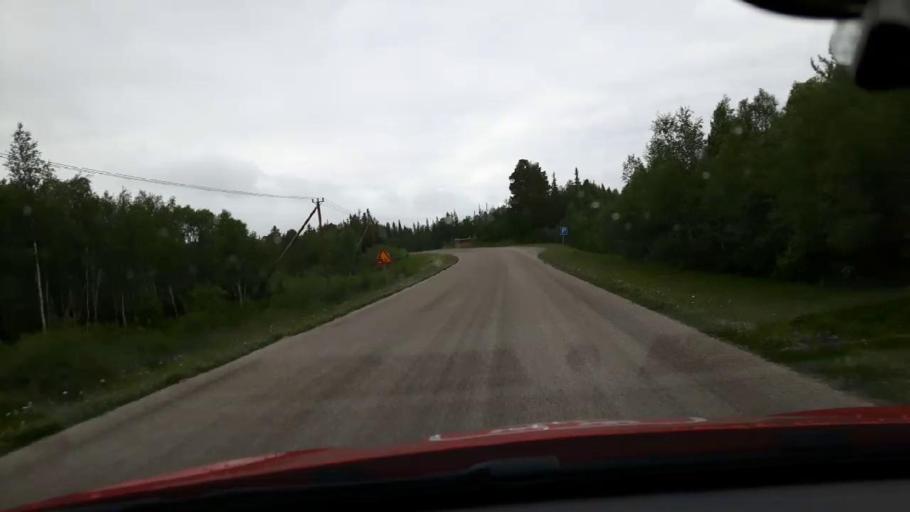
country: NO
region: Nord-Trondelag
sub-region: Meraker
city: Meraker
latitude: 63.2834
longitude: 12.3506
